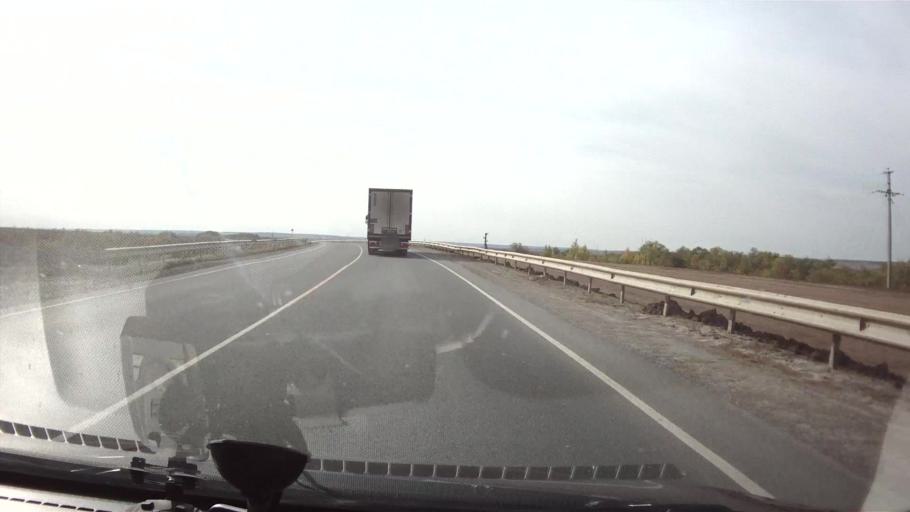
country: RU
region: Saratov
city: Sennoy
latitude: 52.1613
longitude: 47.0495
